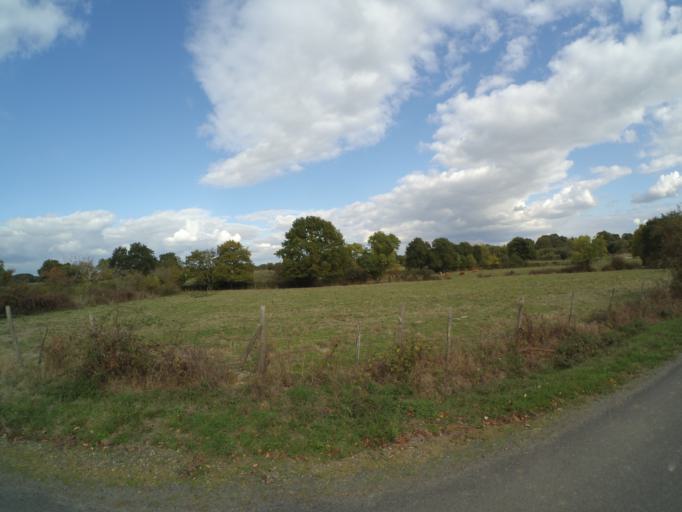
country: FR
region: Pays de la Loire
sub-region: Departement de la Loire-Atlantique
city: Maisdon-sur-Sevre
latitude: 47.0785
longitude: -1.3718
